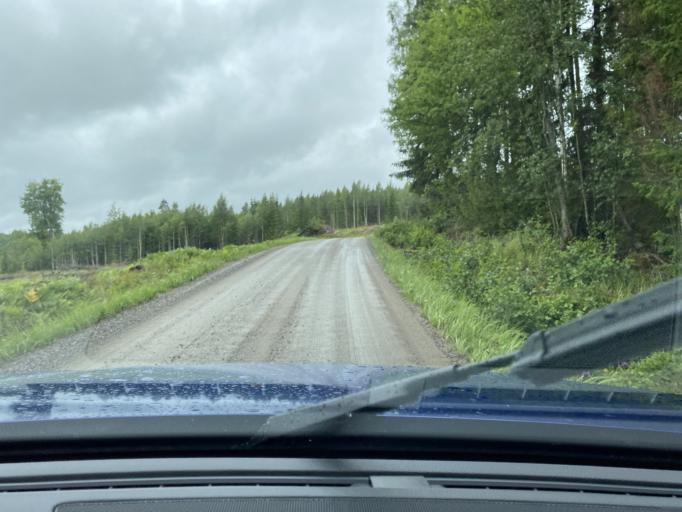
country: FI
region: Pirkanmaa
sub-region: Lounais-Pirkanmaa
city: Punkalaidun
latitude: 61.1474
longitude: 23.2626
